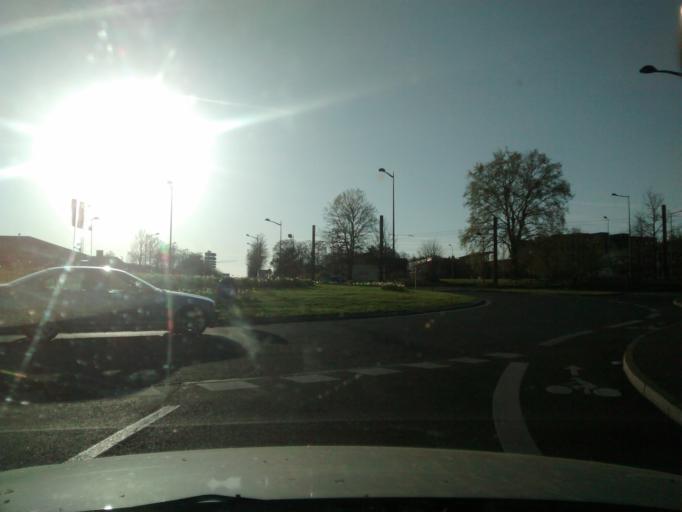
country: FR
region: Pays de la Loire
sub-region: Departement de la Sarthe
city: La Chapelle-Saint-Aubin
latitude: 48.0147
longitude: 0.1620
